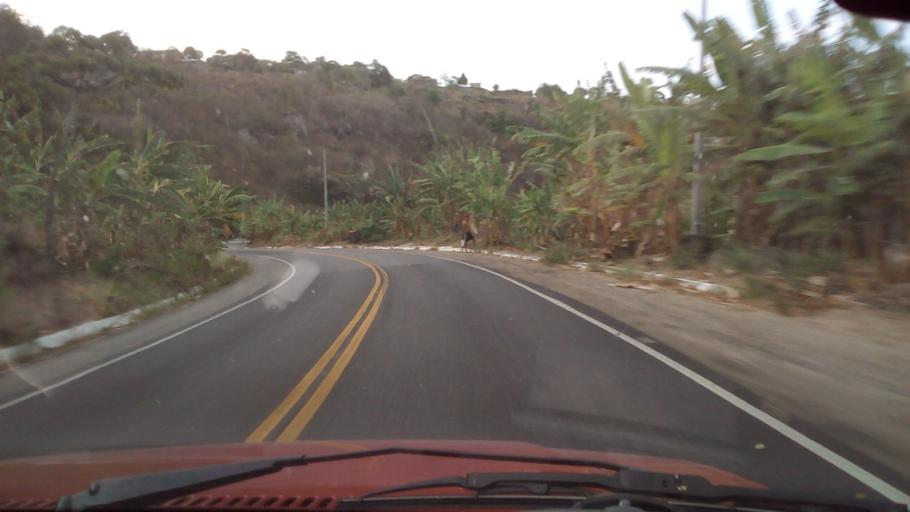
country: BR
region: Paraiba
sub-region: Bananeiras
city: Solanea
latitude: -6.7440
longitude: -35.5632
